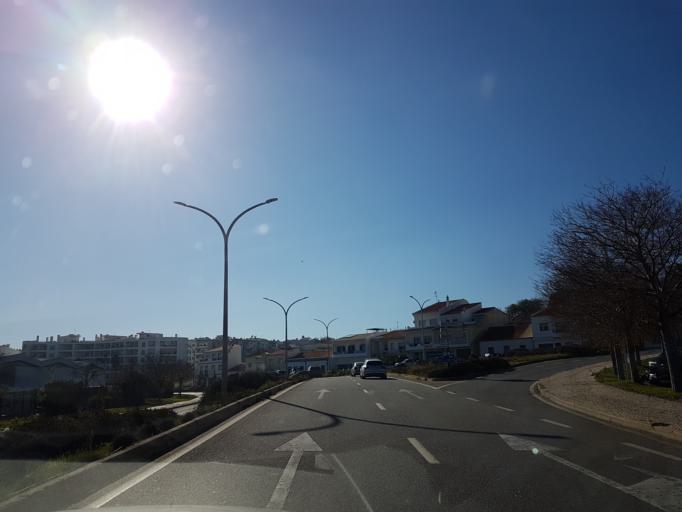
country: PT
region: Faro
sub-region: Lagos
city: Lagos
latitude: 37.1133
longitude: -8.6813
